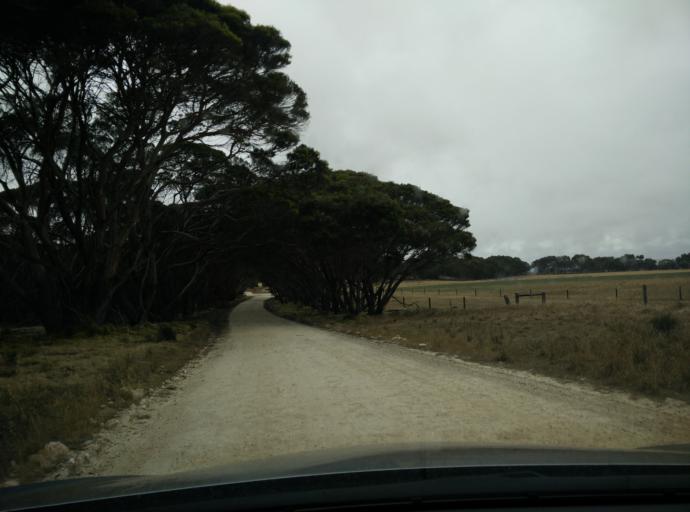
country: AU
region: South Australia
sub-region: Kangaroo Island
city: Kingscote
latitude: -35.8486
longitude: 137.5437
